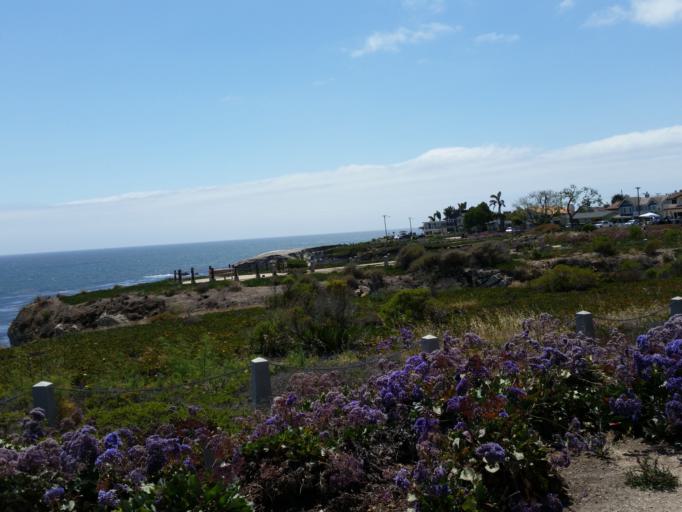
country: US
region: California
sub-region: San Luis Obispo County
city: Pismo Beach
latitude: 35.1535
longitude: -120.6651
